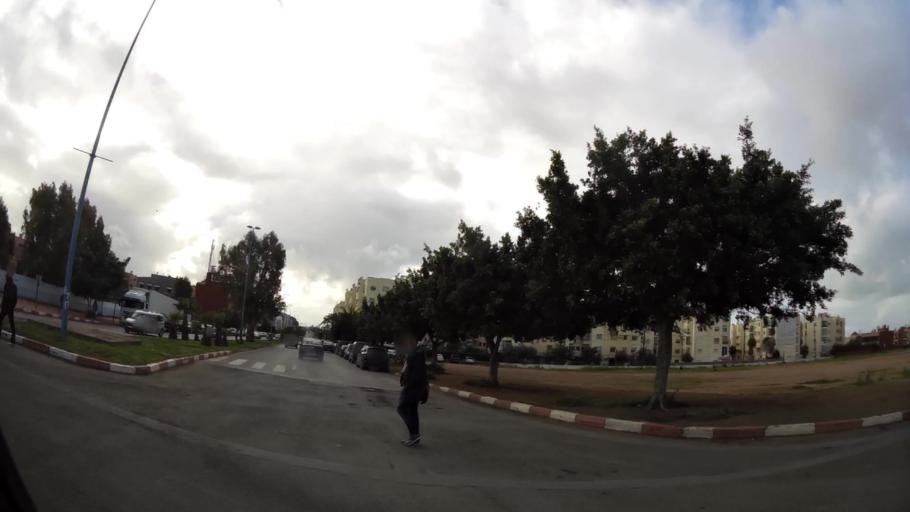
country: MA
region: Grand Casablanca
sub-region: Mohammedia
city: Mohammedia
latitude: 33.6927
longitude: -7.3753
